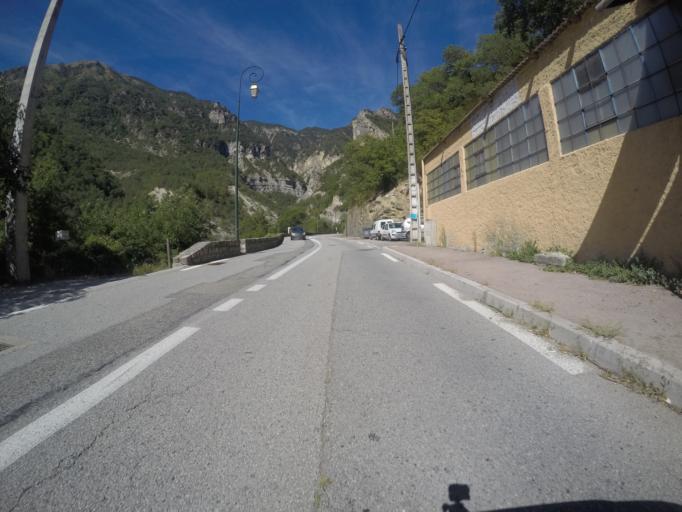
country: FR
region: Provence-Alpes-Cote d'Azur
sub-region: Departement des Alpes-Maritimes
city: Gilette
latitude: 43.9729
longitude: 7.1435
